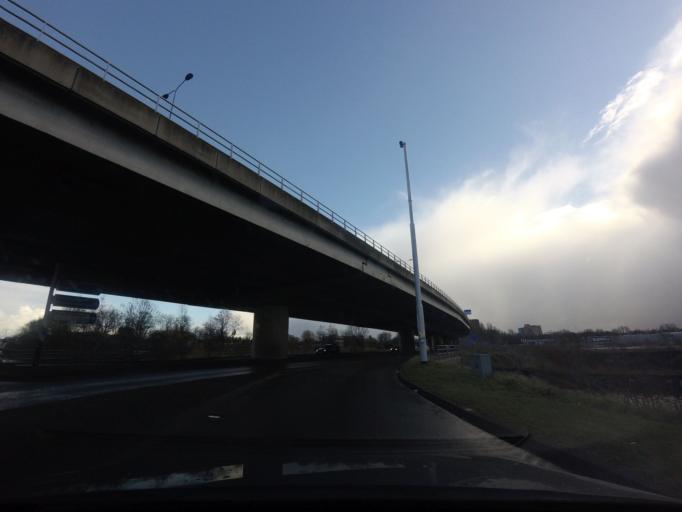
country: NL
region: Groningen
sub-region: Gemeente Groningen
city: Groningen
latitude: 53.2129
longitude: 6.5418
